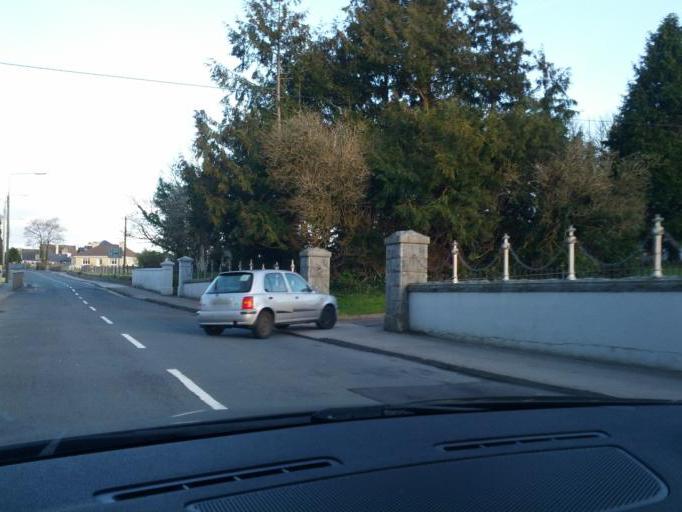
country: IE
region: Connaught
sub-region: Sligo
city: Tobercurry
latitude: 54.0535
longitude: -8.7269
